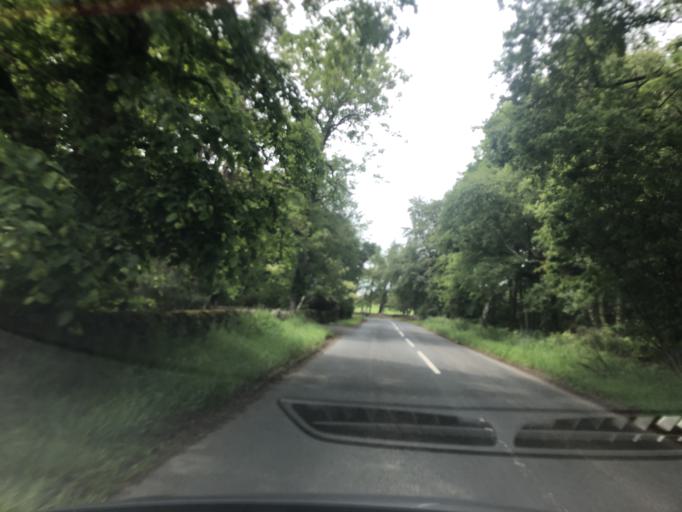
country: GB
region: Scotland
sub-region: The Scottish Borders
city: West Linton
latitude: 55.7394
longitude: -3.3345
